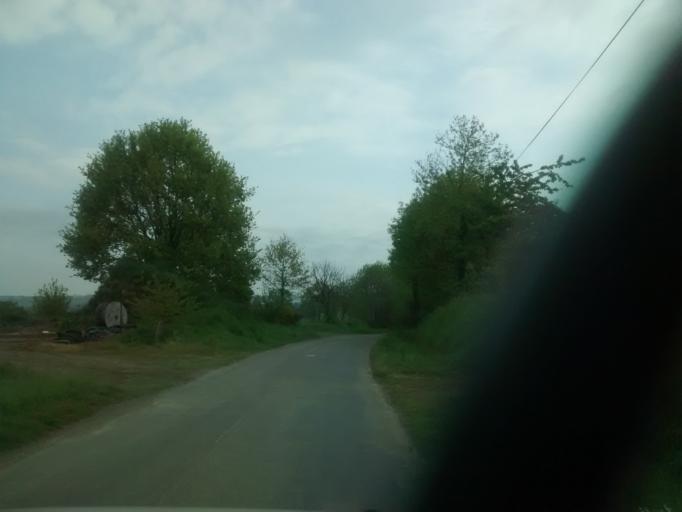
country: FR
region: Brittany
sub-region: Departement d'Ille-et-Vilaine
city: Saint-Jean-sur-Couesnon
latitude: 48.2771
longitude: -1.3135
